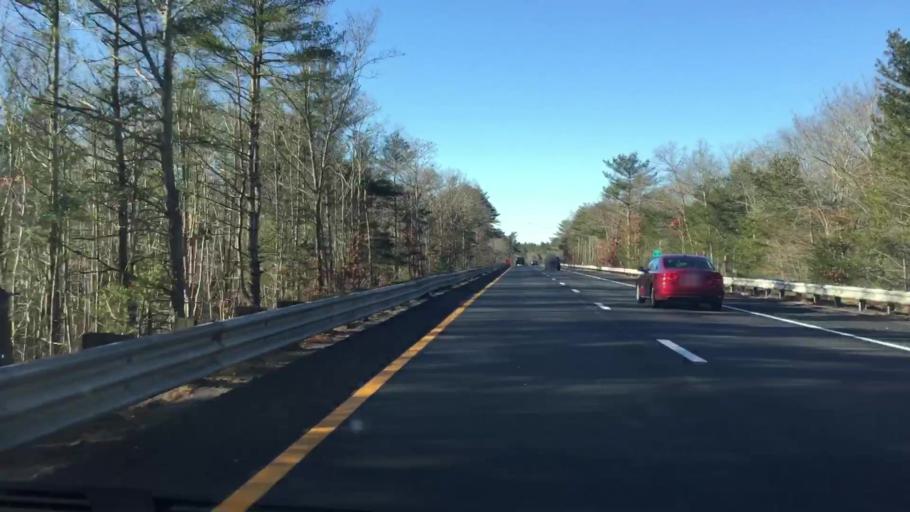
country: US
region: Massachusetts
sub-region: Plymouth County
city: West Wareham
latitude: 41.8114
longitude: -70.7854
